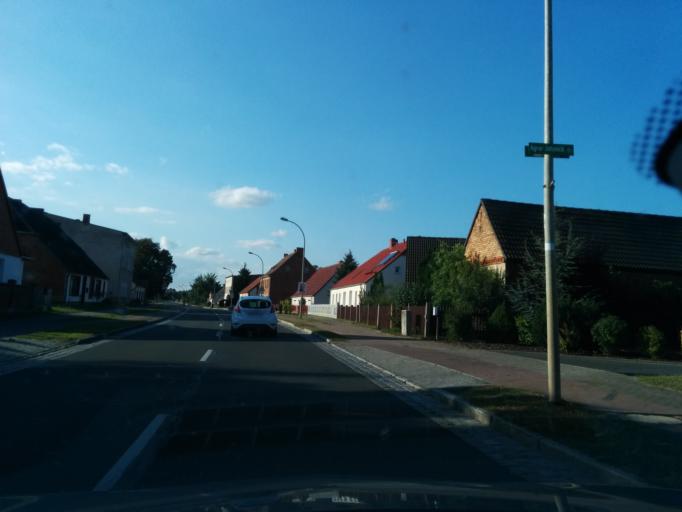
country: DE
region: Mecklenburg-Vorpommern
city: Jatznick
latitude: 53.5763
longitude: 13.9452
